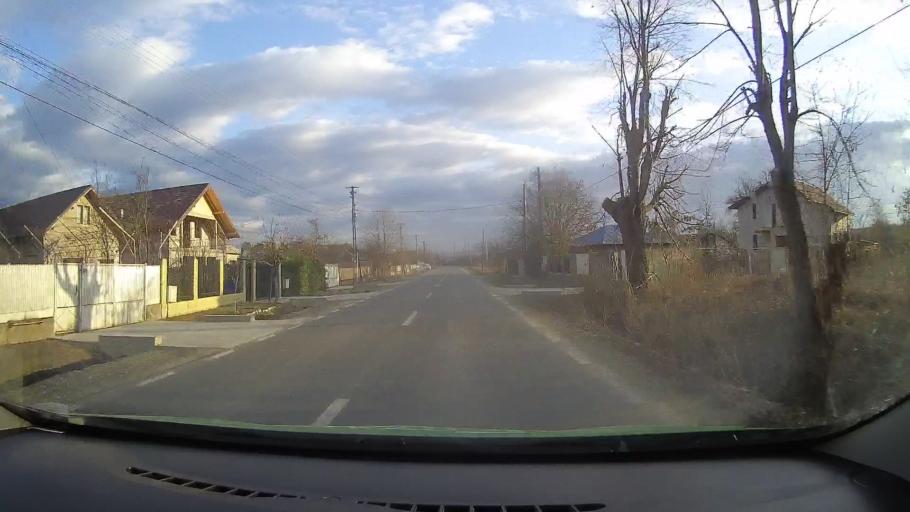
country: RO
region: Dambovita
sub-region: Comuna I. L. Caragiale
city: Ghirdoveni
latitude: 44.9540
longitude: 25.6578
